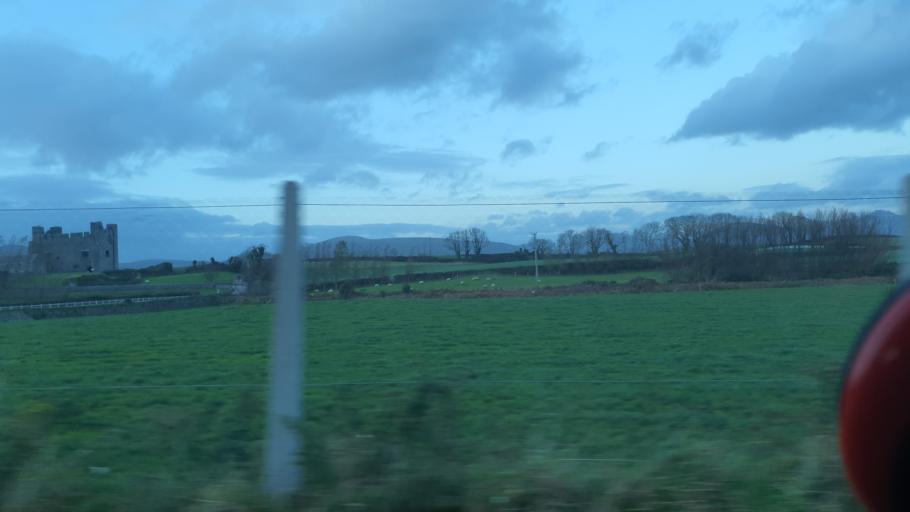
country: IE
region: Leinster
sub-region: Lu
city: Carlingford
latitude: 54.0388
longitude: -6.0954
